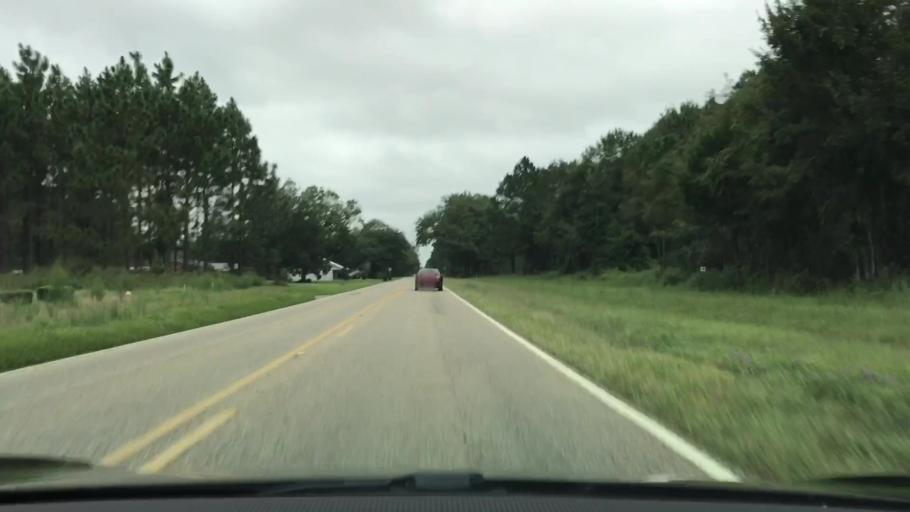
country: US
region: Alabama
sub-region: Geneva County
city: Samson
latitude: 31.1914
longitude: -86.1554
